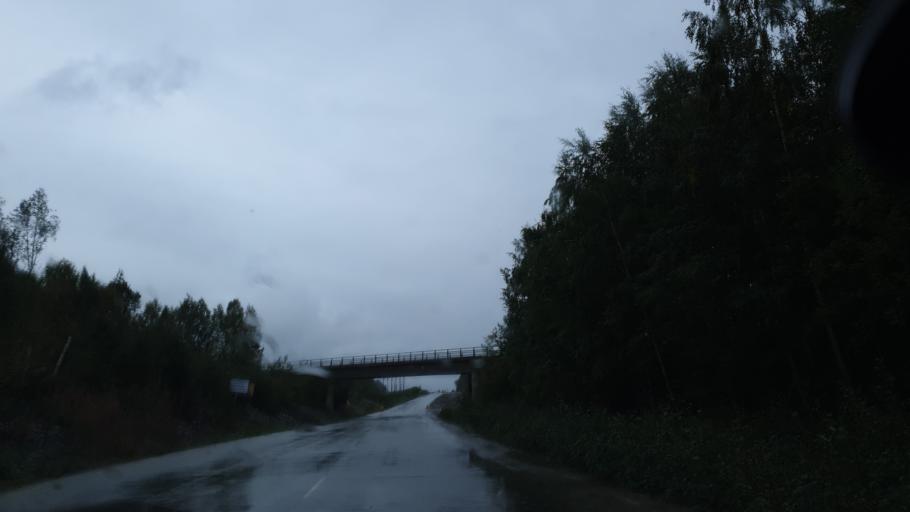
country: SE
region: Vaesterbotten
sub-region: Skelleftea Kommun
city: Soedra Bergsbyn
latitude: 64.7444
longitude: 21.0585
